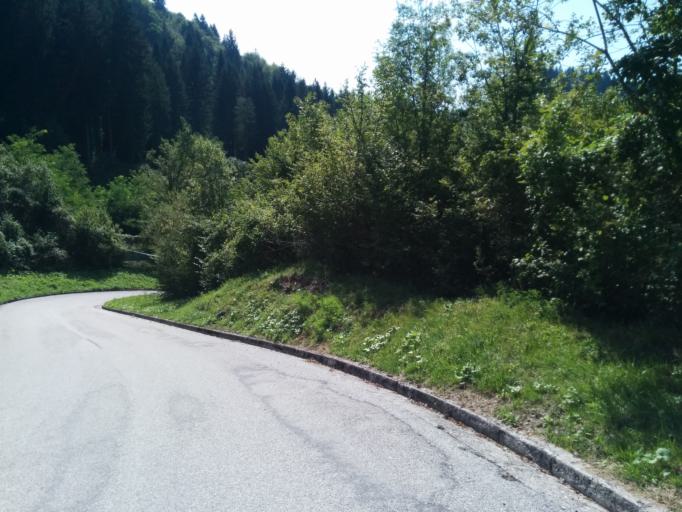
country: IT
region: Friuli Venezia Giulia
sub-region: Provincia di Udine
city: Ovaro
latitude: 46.4657
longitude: 12.8746
